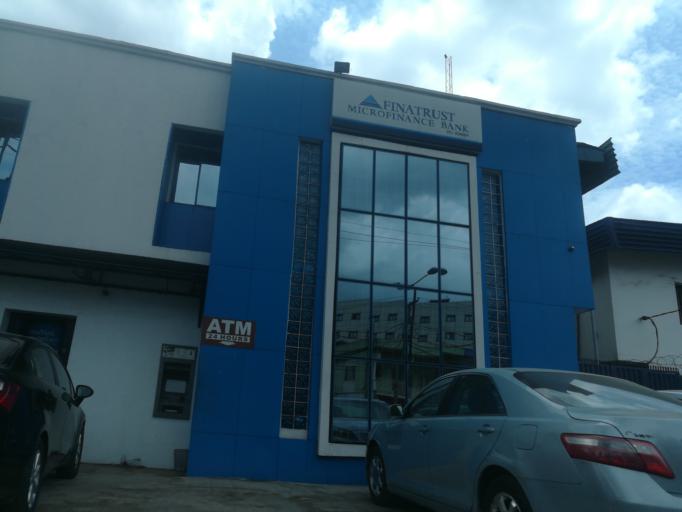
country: NG
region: Lagos
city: Ikeja
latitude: 6.5959
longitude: 3.3519
